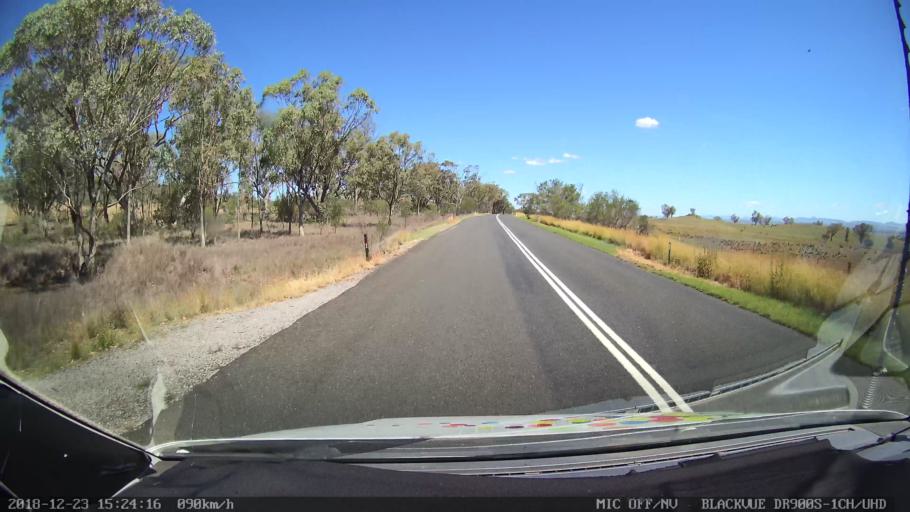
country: AU
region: New South Wales
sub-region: Tamworth Municipality
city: Manilla
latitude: -30.8897
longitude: 150.8220
